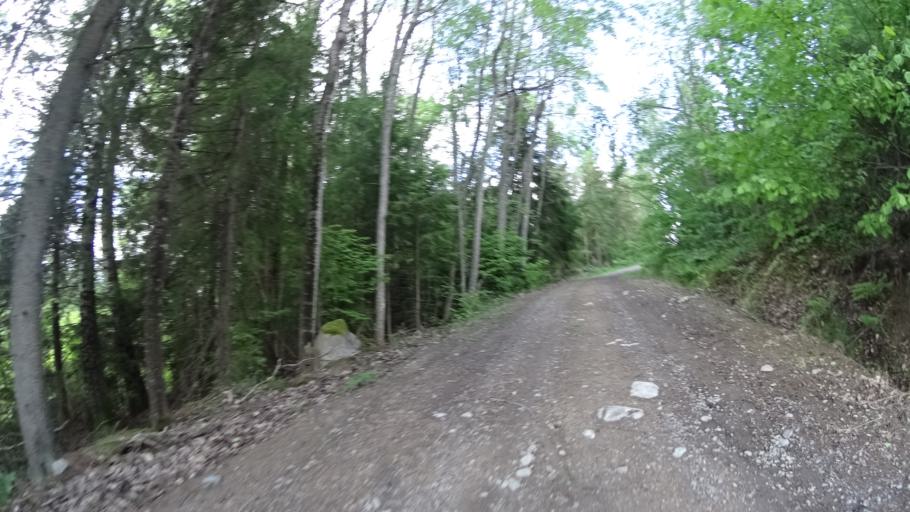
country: FI
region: Uusimaa
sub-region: Raaseporin
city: Karis
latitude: 60.1520
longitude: 23.6234
